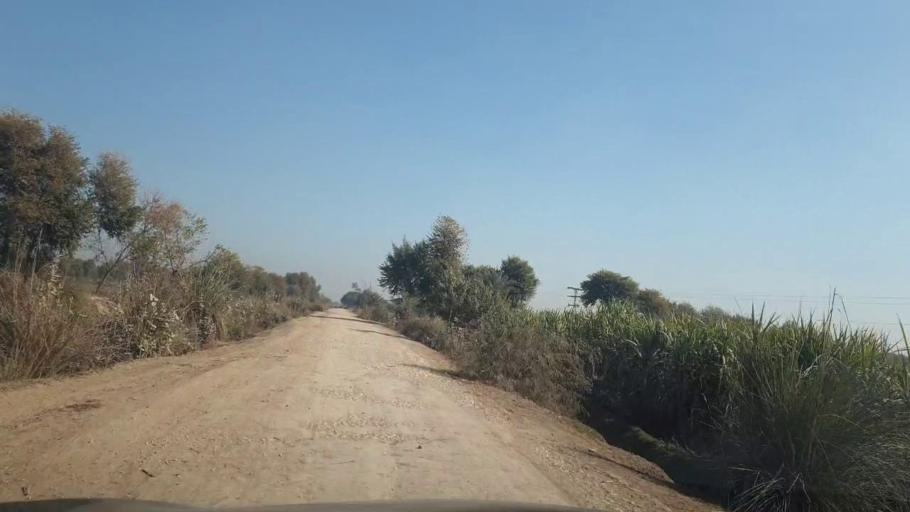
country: PK
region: Sindh
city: Mirpur Mathelo
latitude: 28.1286
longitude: 69.4991
